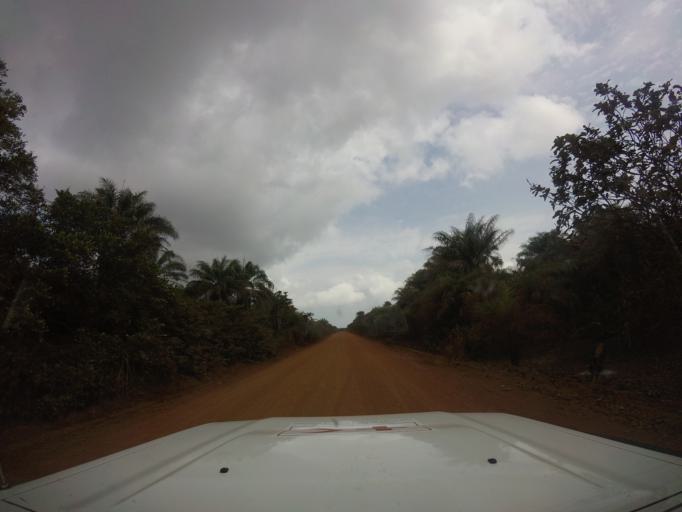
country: LR
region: Grand Cape Mount
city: Robertsport
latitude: 6.6978
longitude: -11.2861
